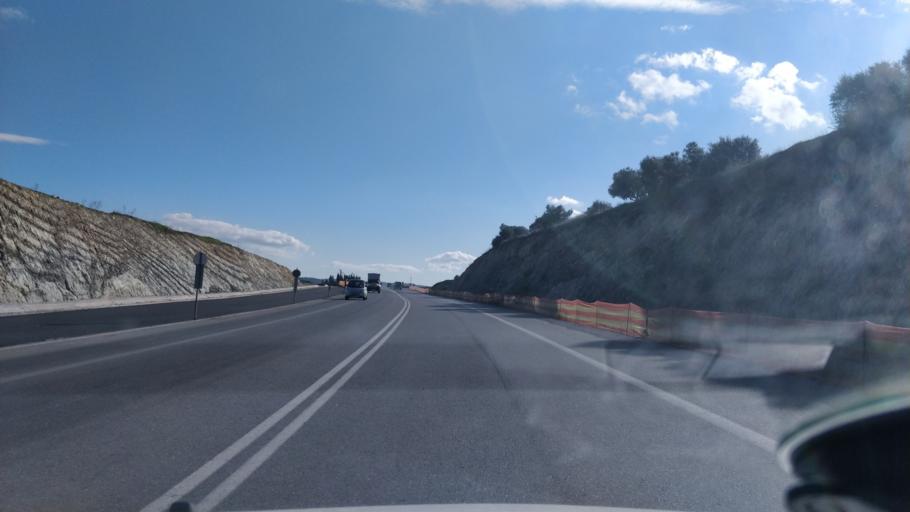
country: GR
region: Crete
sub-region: Nomos Irakleiou
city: Ano Arhanes
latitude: 35.2330
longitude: 25.1792
